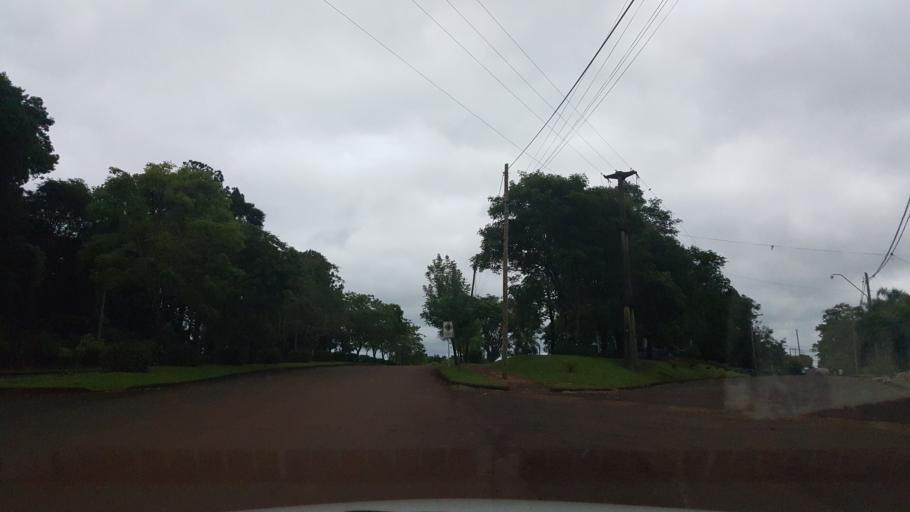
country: AR
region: Misiones
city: Ruiz de Montoya
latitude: -26.9795
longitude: -55.0498
